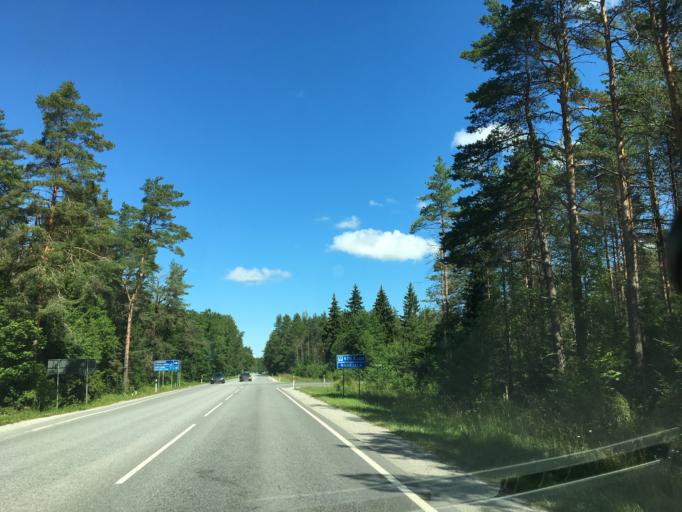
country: EE
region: Harju
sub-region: Nissi vald
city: Riisipere
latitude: 59.2432
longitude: 24.2776
